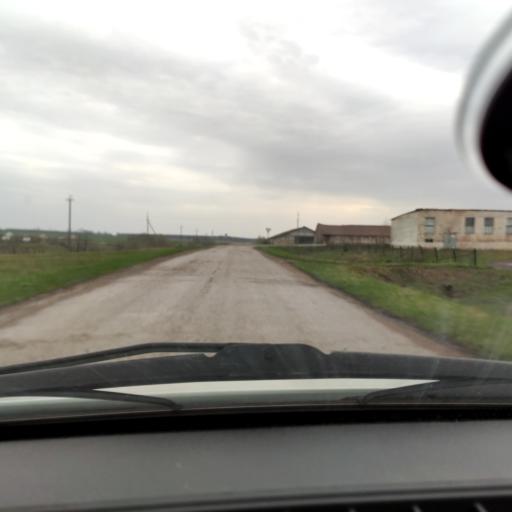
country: RU
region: Bashkortostan
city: Tolbazy
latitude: 54.1697
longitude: 55.9463
